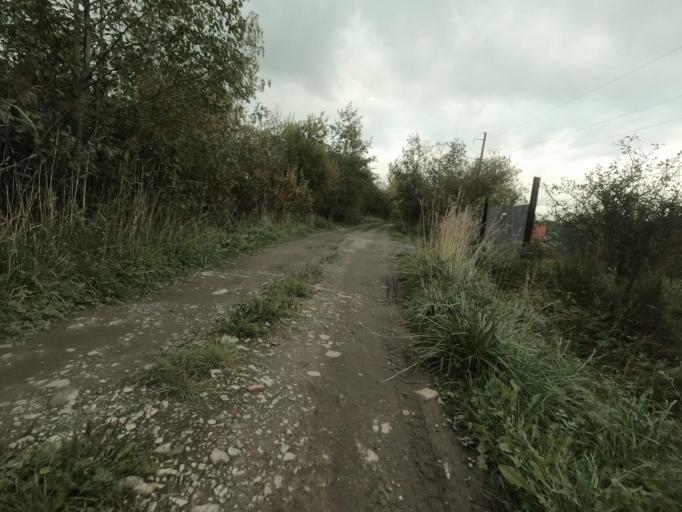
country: RU
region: St.-Petersburg
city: Sapernyy
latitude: 59.7758
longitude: 30.6462
